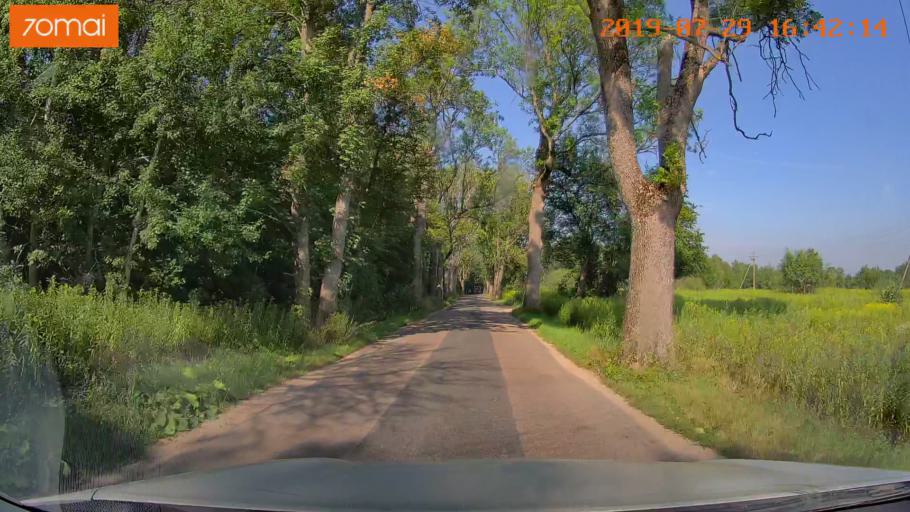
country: RU
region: Kaliningrad
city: Primorsk
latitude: 54.7416
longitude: 20.0710
